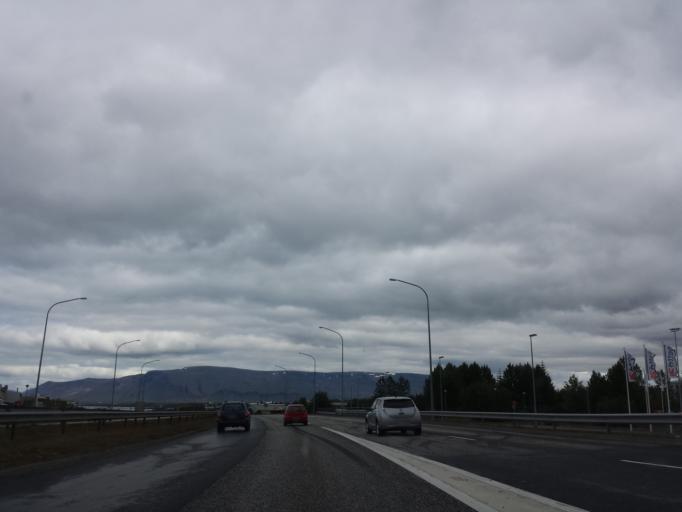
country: IS
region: Capital Region
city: Reykjavik
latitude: 64.1088
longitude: -21.8458
